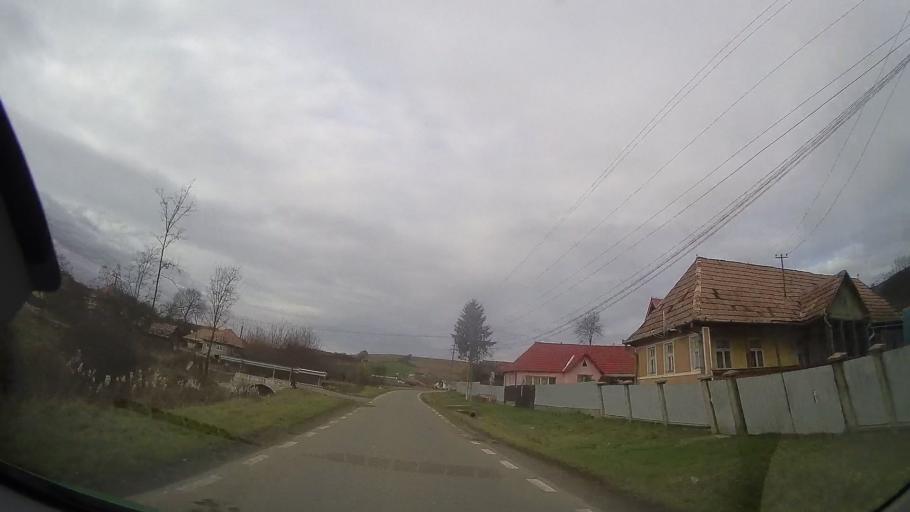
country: RO
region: Mures
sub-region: Comuna Cozma
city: Cozma
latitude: 46.8110
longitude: 24.5040
